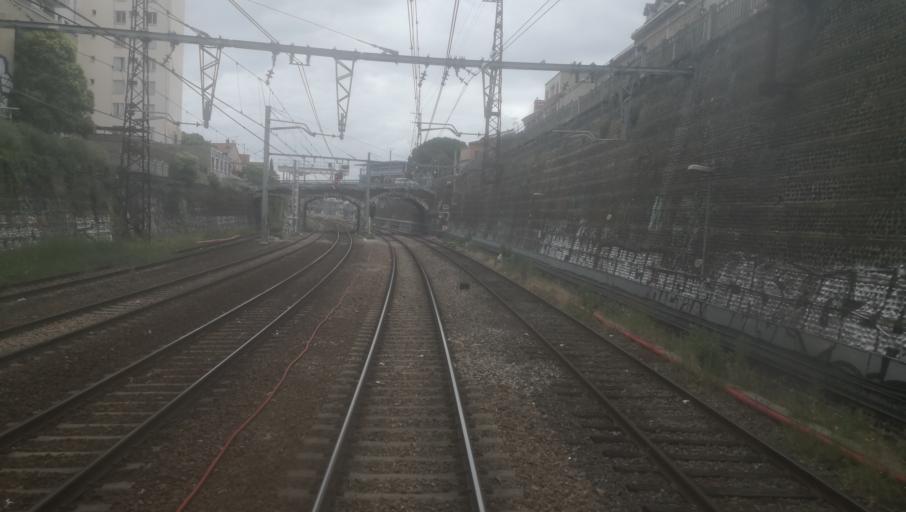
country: FR
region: Midi-Pyrenees
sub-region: Departement de la Haute-Garonne
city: Toulouse
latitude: 43.6056
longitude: 1.4576
